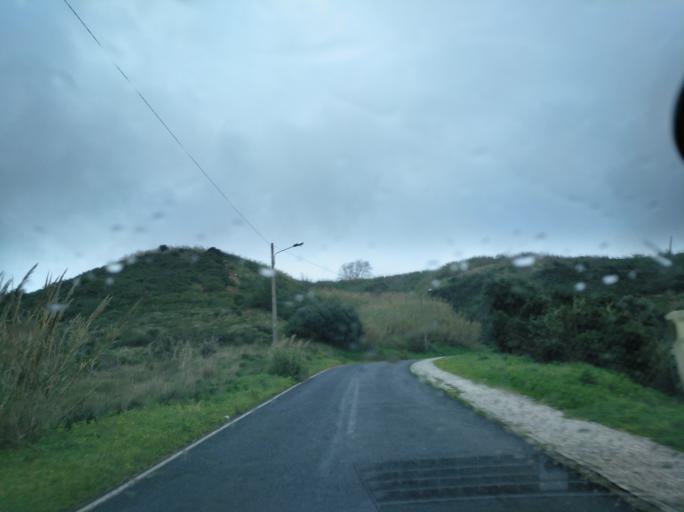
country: PT
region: Lisbon
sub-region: Odivelas
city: Pontinha
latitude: 38.7726
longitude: -9.1942
